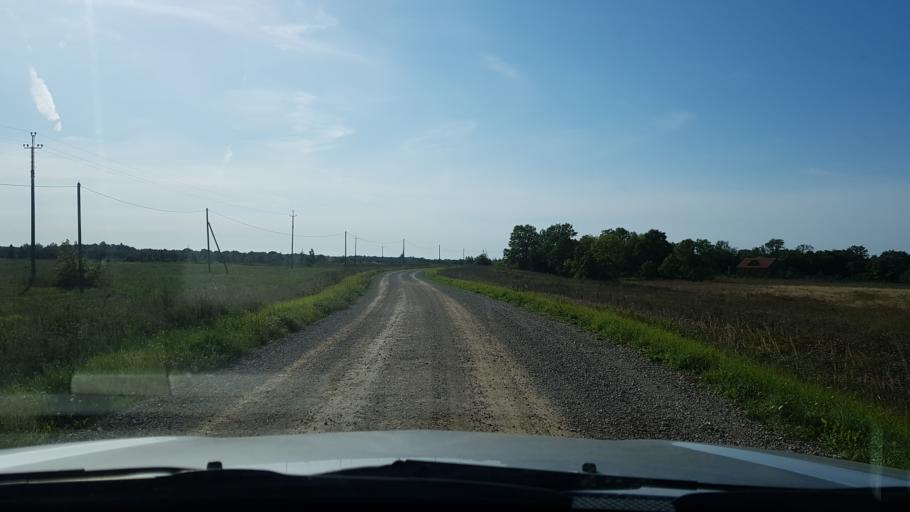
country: EE
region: Ida-Virumaa
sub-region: Narva-Joesuu linn
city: Narva-Joesuu
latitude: 59.4091
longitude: 28.0243
